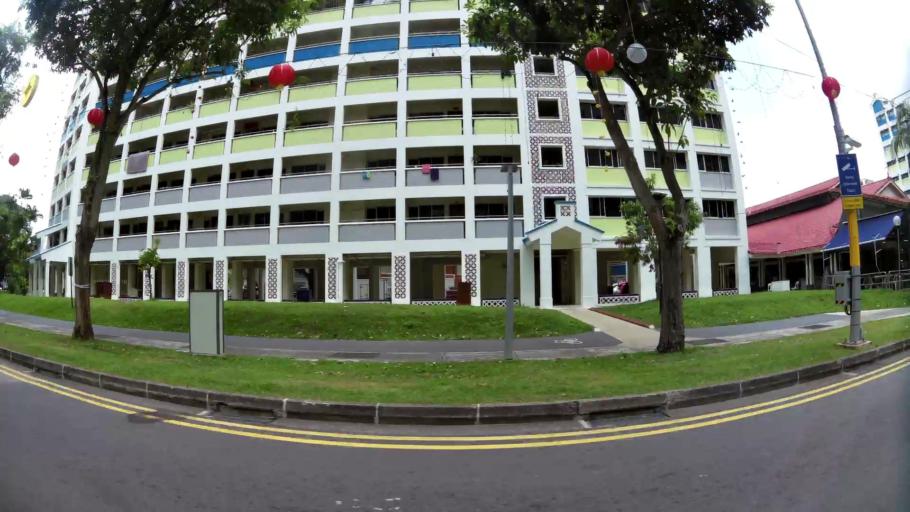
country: MY
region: Johor
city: Kampung Pasir Gudang Baru
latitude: 1.4235
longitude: 103.8464
